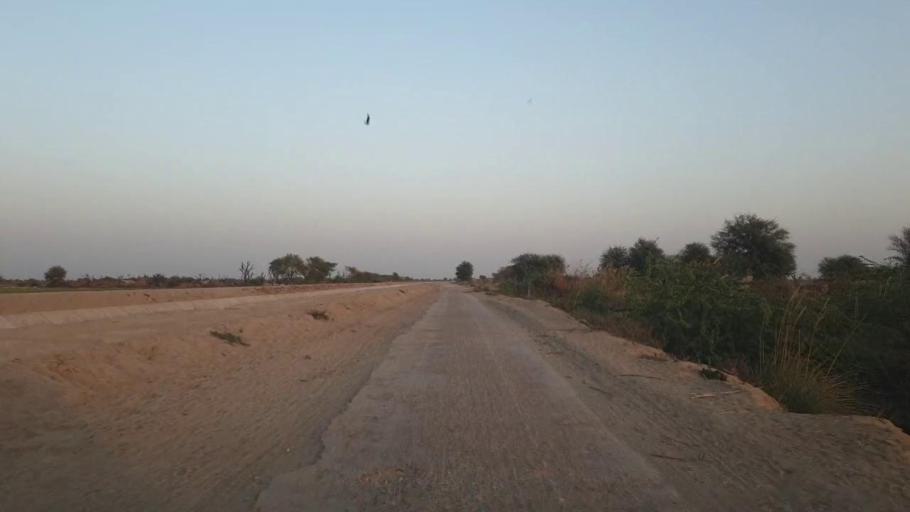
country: PK
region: Sindh
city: Dhoro Naro
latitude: 25.4580
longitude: 69.6072
